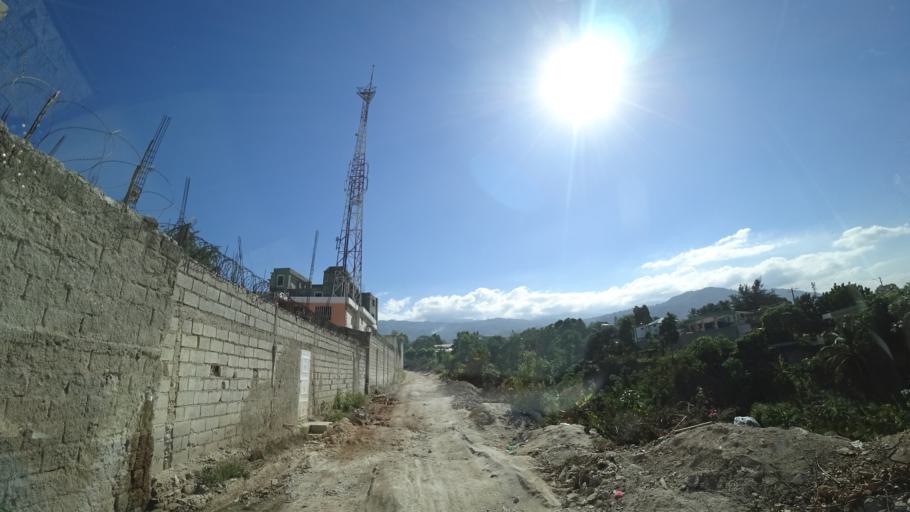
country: HT
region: Ouest
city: Delmas 73
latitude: 18.5392
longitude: -72.2863
